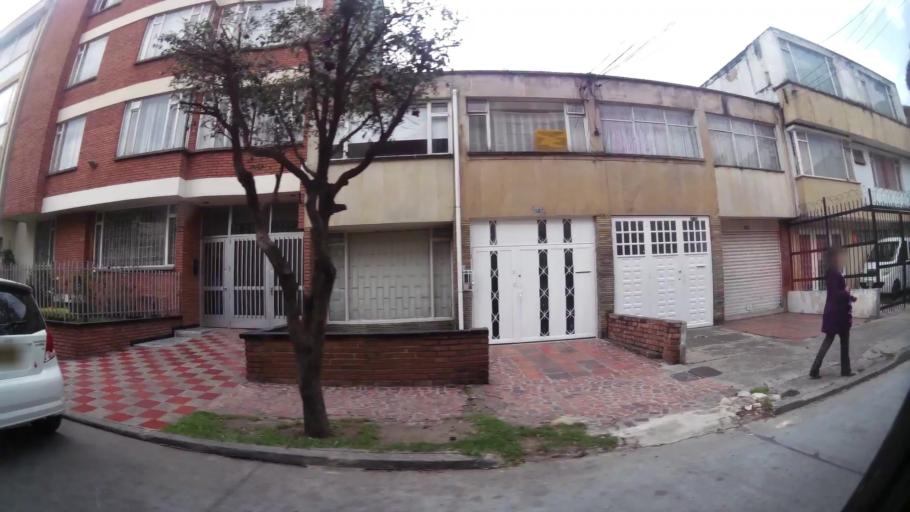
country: CO
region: Bogota D.C.
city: Bogota
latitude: 4.6327
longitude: -74.0780
